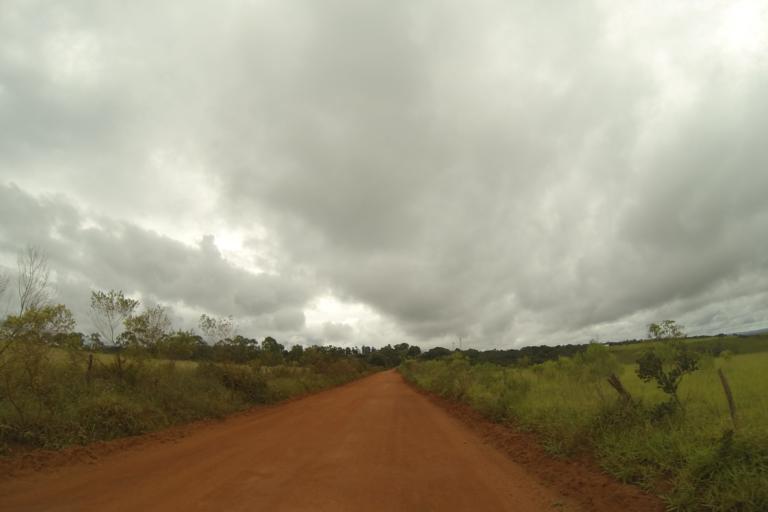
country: BR
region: Minas Gerais
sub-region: Campos Altos
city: Campos Altos
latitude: -19.8729
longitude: -46.3040
